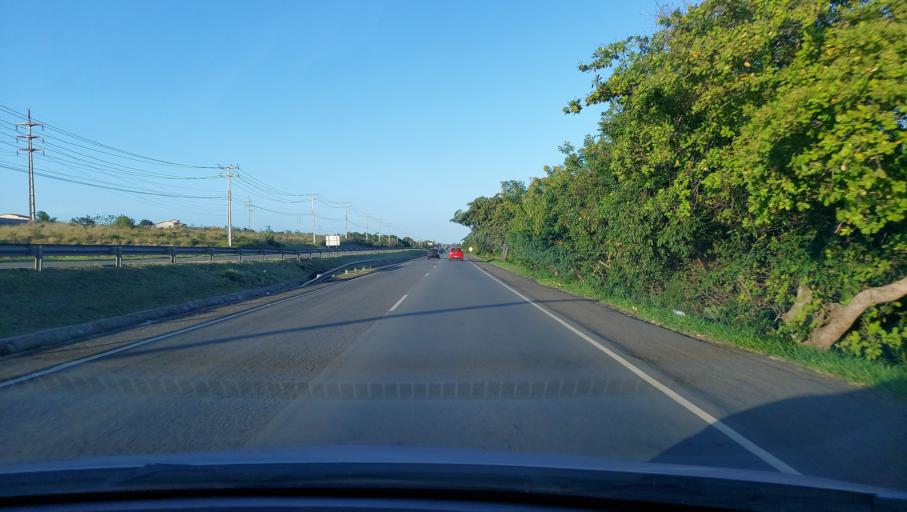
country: BR
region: Bahia
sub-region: Camacari
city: Camacari
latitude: -12.7927
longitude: -38.2079
